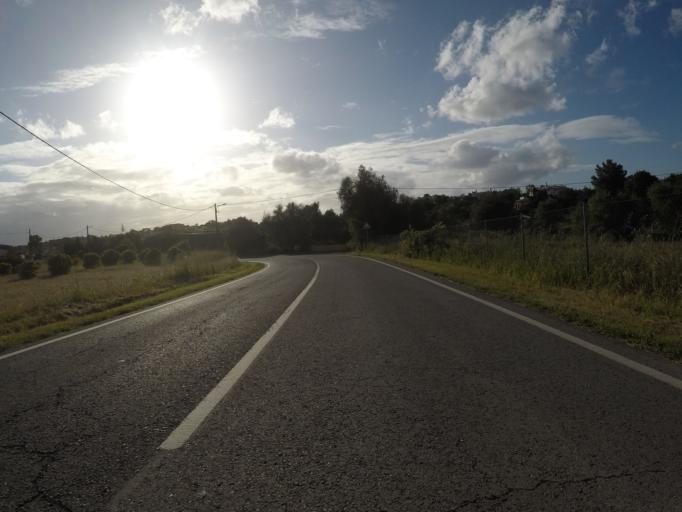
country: PT
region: Faro
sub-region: Lagoa
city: Carvoeiro
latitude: 37.1126
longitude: -8.4511
